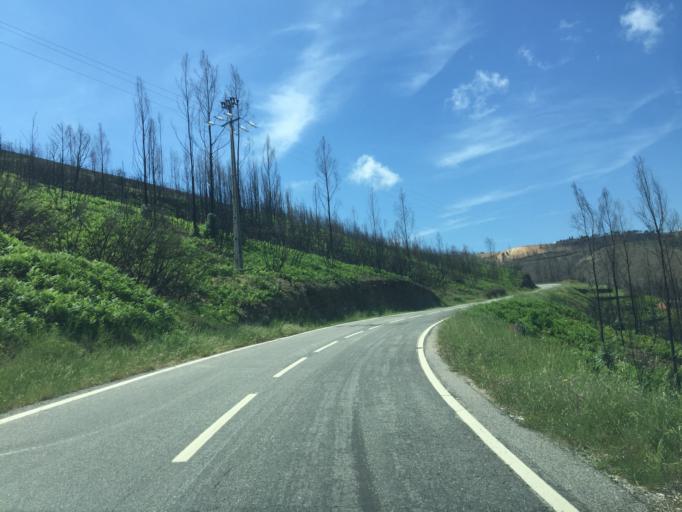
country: PT
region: Coimbra
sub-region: Pampilhosa da Serra
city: Pampilhosa da Serra
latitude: 40.0386
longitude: -7.9583
